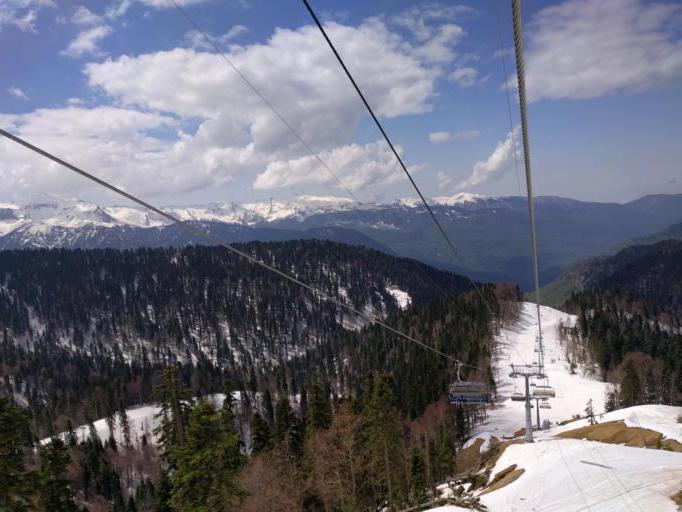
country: RU
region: Krasnodarskiy
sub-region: Sochi City
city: Krasnaya Polyana
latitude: 43.6185
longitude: 40.3024
